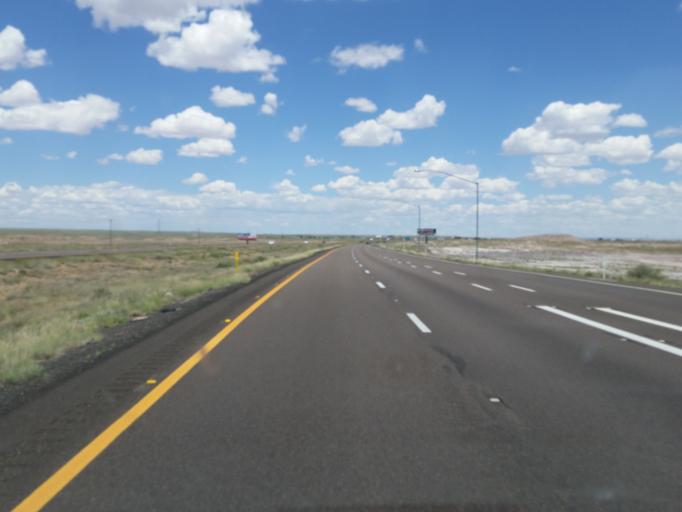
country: US
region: Arizona
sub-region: Navajo County
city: Holbrook
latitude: 34.9750
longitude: -110.0820
